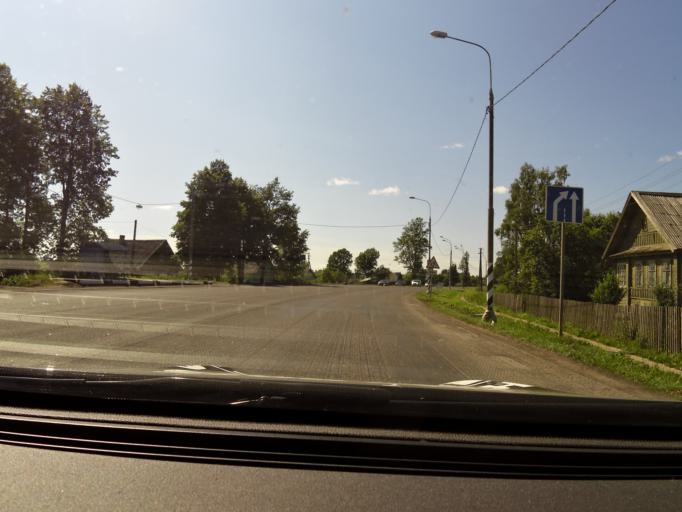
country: RU
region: Novgorod
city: Proletariy
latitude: 58.3670
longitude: 32.0688
